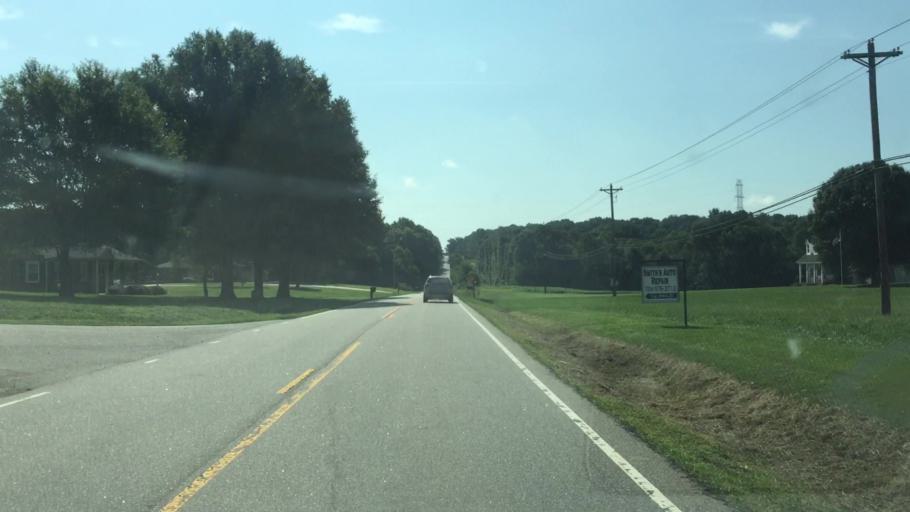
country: US
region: North Carolina
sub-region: Union County
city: Fairview
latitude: 35.1353
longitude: -80.4940
